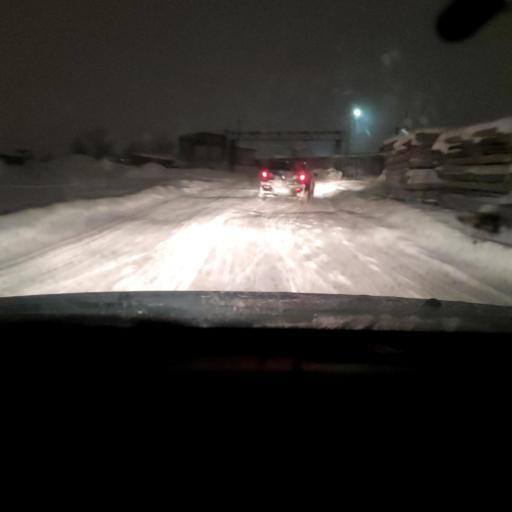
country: RU
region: Perm
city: Kondratovo
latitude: 58.0194
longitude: 56.1398
